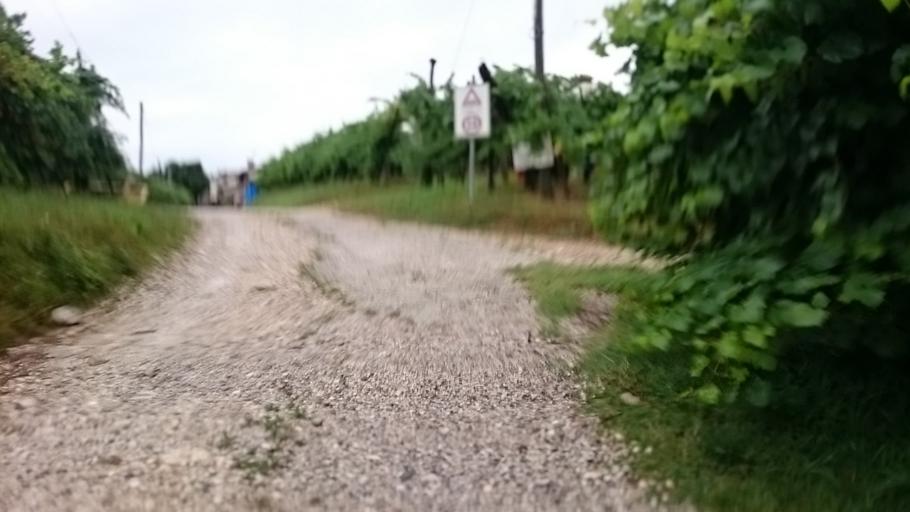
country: IT
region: Veneto
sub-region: Provincia di Treviso
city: Monfumo
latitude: 45.8204
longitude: 11.9161
